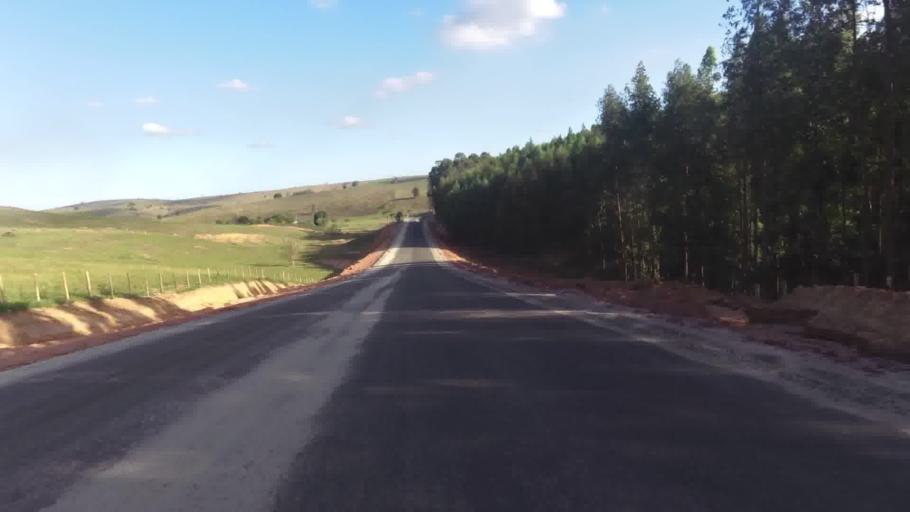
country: BR
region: Espirito Santo
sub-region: Marataizes
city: Marataizes
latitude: -21.1261
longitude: -41.0498
